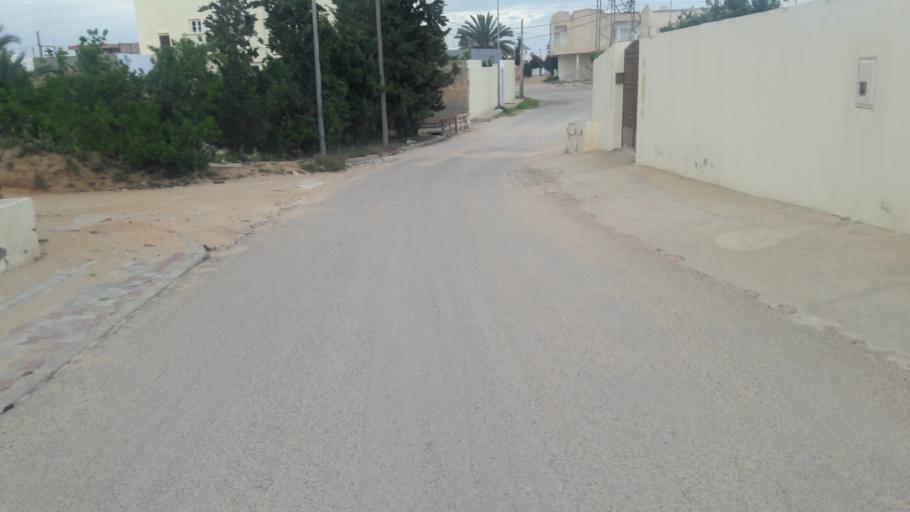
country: TN
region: Safaqis
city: Al Qarmadah
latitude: 34.8101
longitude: 10.7484
